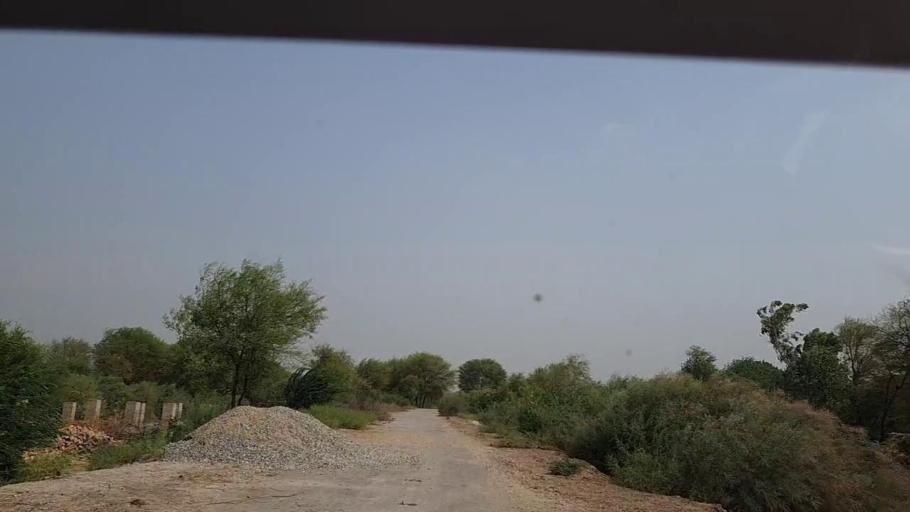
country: PK
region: Sindh
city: Khairpur Nathan Shah
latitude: 27.0315
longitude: 67.6732
